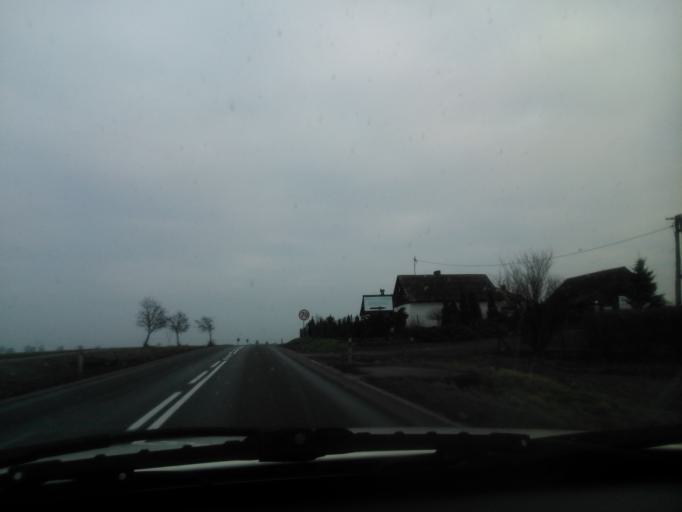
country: PL
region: Kujawsko-Pomorskie
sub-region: Powiat torunski
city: Lysomice
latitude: 53.0706
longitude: 18.6820
